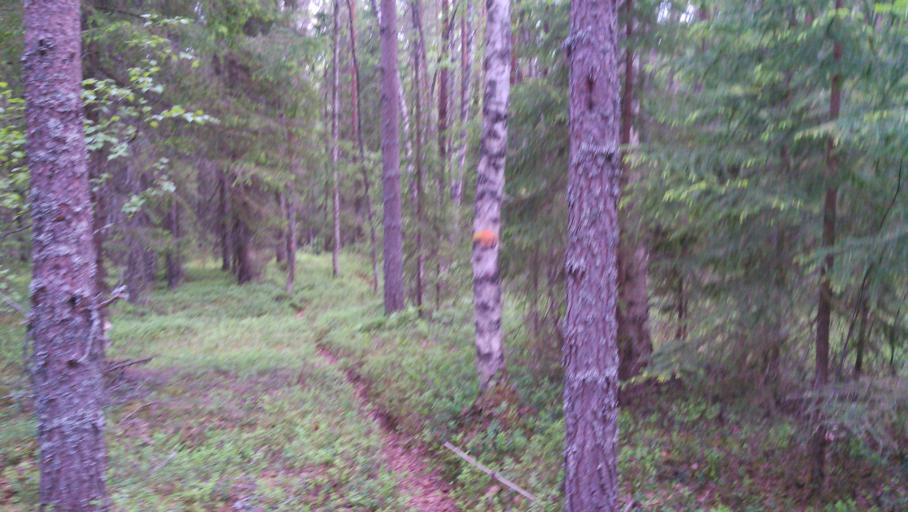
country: SE
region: Vaesterbotten
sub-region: Vannas Kommun
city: Vannasby
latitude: 64.0118
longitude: 19.9188
